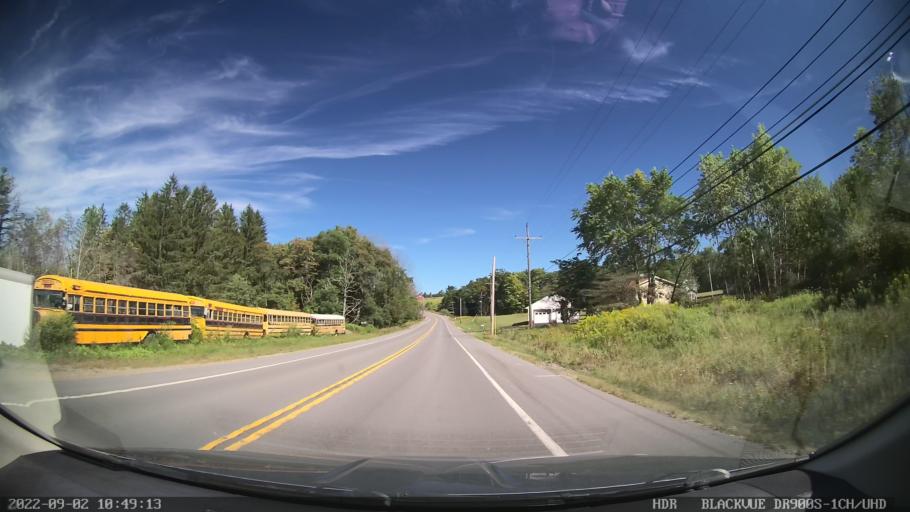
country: US
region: Pennsylvania
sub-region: Tioga County
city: Blossburg
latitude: 41.5974
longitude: -77.1103
